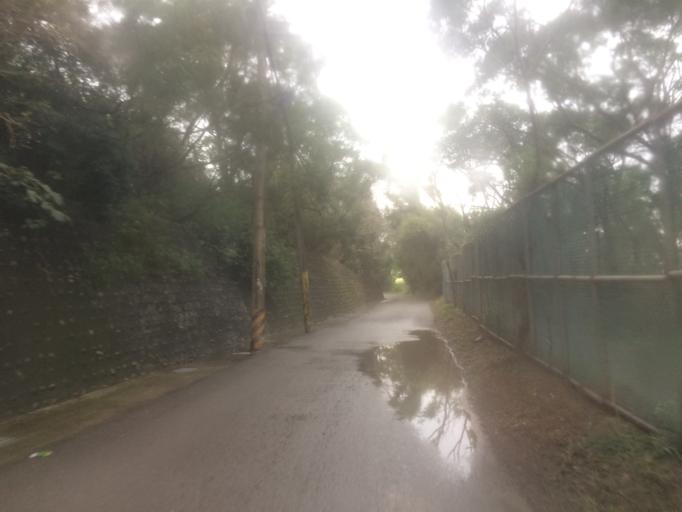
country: TW
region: Taiwan
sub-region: Hsinchu
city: Hsinchu
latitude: 24.7648
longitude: 120.9667
